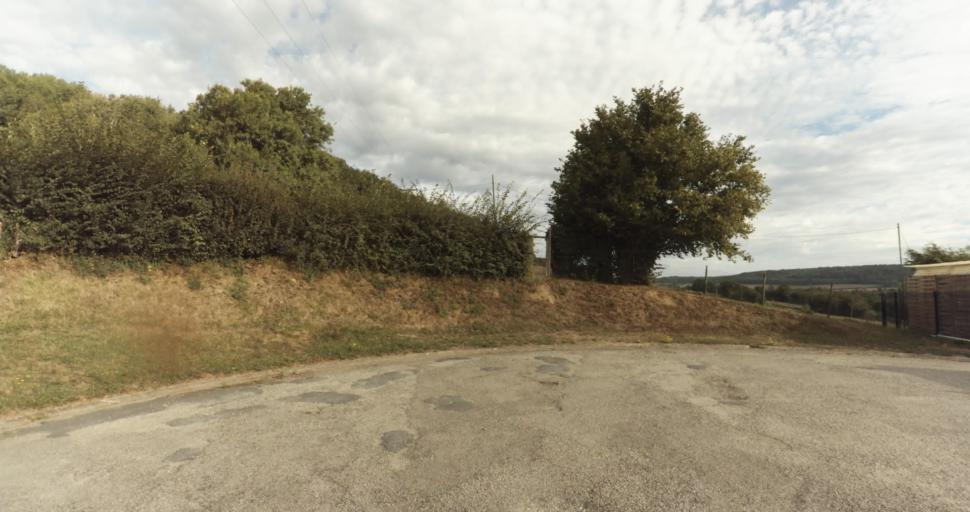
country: FR
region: Lower Normandy
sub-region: Departement de l'Orne
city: Vimoutiers
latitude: 48.9319
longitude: 0.2660
